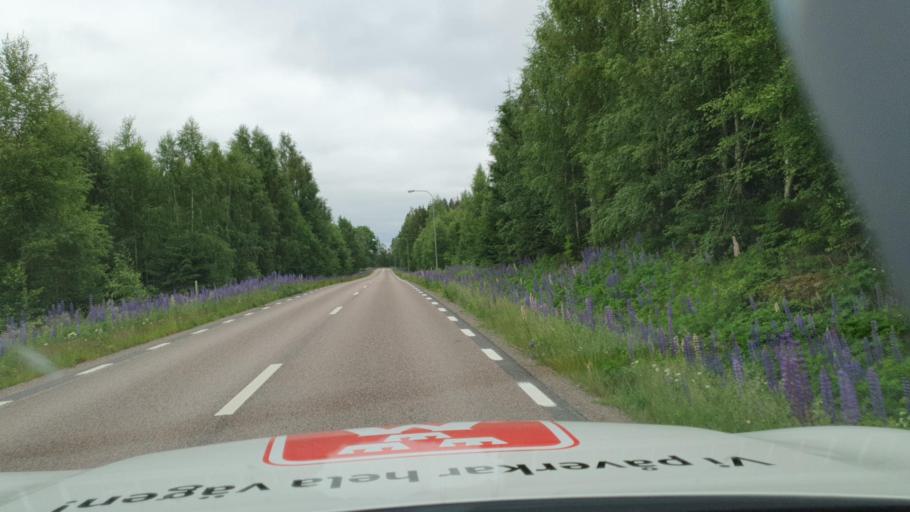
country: SE
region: Vaermland
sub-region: Sunne Kommun
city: Sunne
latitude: 59.8788
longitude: 12.9306
